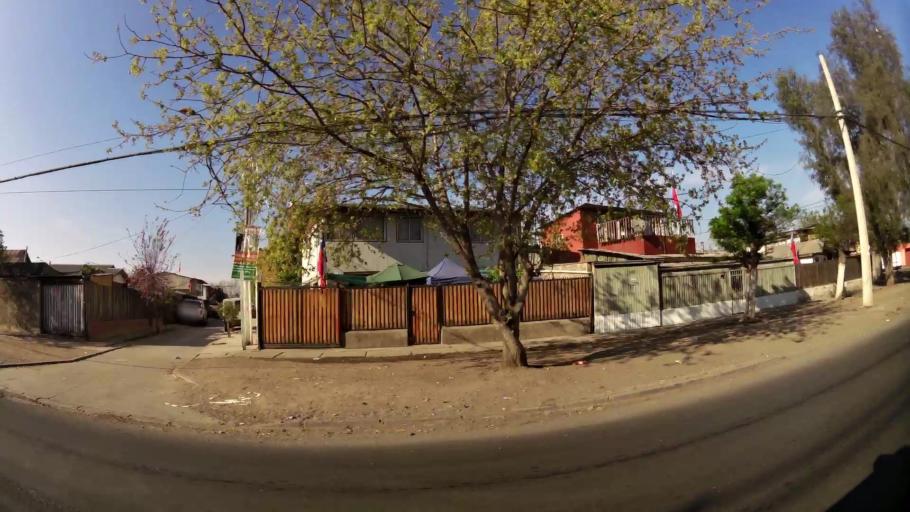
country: CL
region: Santiago Metropolitan
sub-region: Provincia de Santiago
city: Santiago
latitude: -33.3837
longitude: -70.6670
